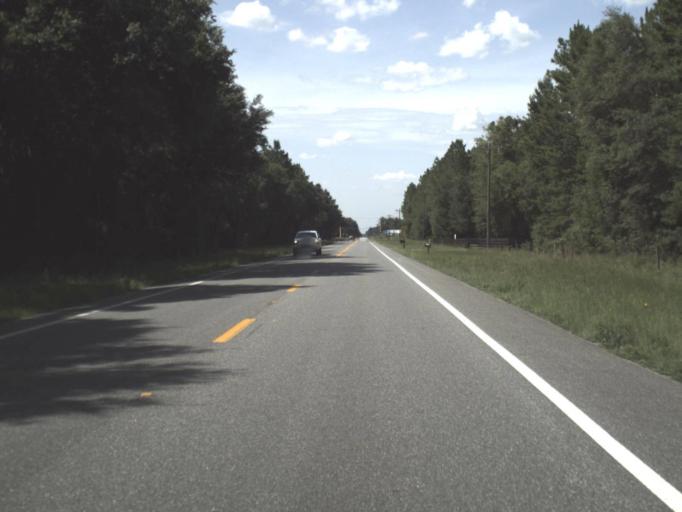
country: US
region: Florida
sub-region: Alachua County
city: High Springs
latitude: 29.8038
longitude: -82.7412
